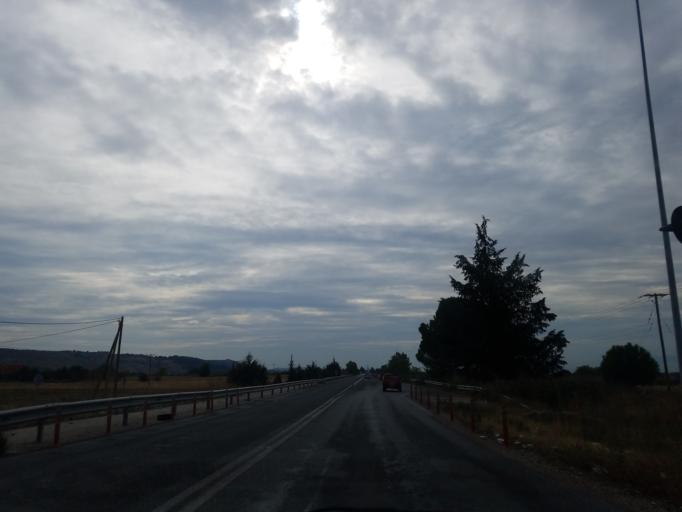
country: GR
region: Thessaly
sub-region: Trikala
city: Vasiliki
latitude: 39.6614
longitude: 21.6740
